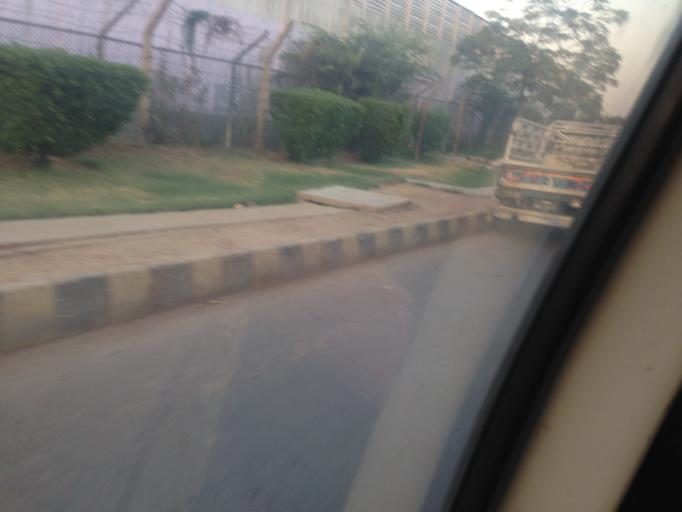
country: PK
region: Sindh
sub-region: Karachi District
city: Karachi
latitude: 24.8753
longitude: 67.0968
